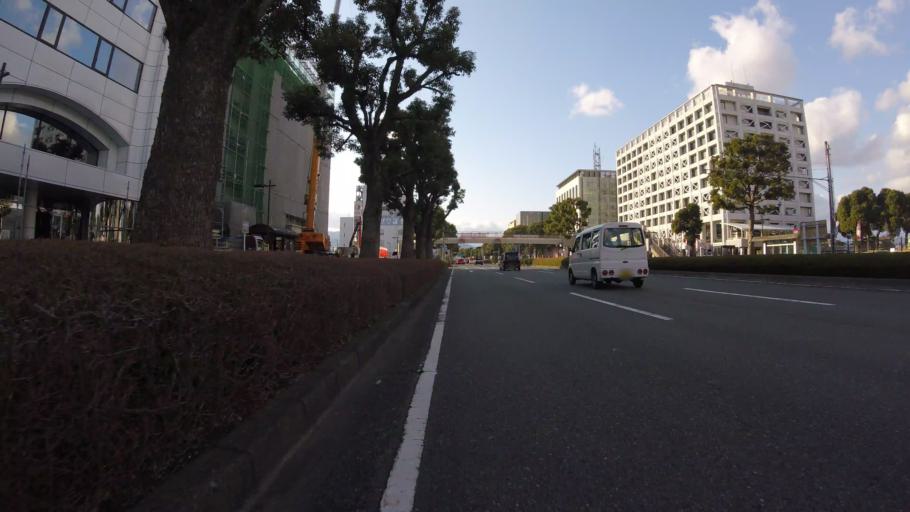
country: JP
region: Shizuoka
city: Fuji
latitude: 35.1606
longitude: 138.6772
